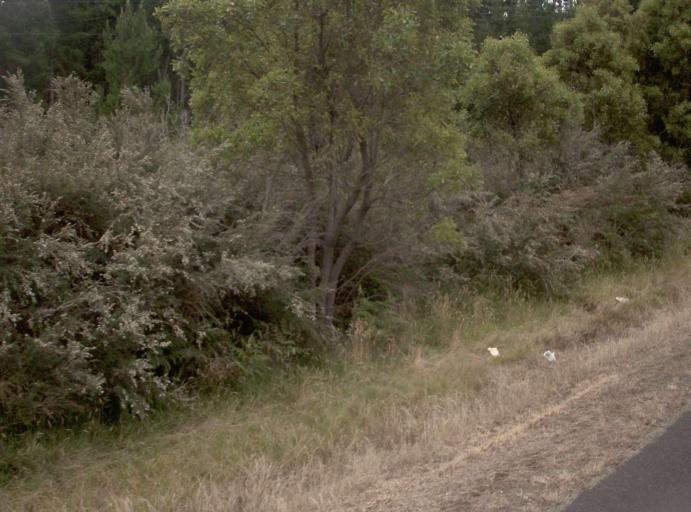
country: AU
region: Victoria
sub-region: Wellington
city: Sale
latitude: -38.2160
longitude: 147.0613
